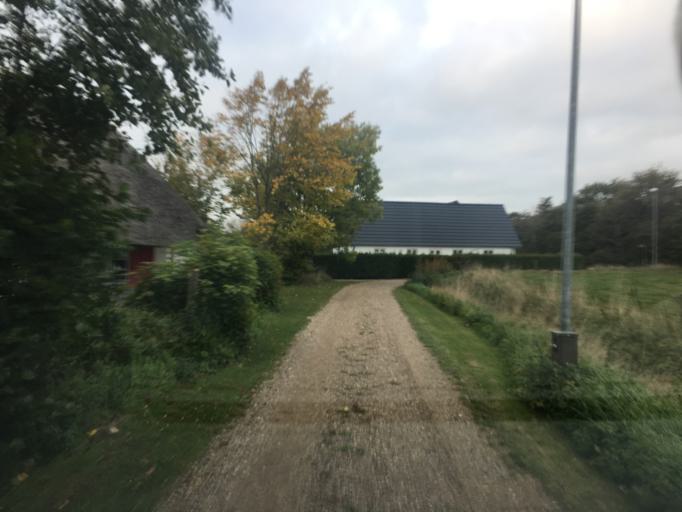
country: DE
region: Schleswig-Holstein
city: Aventoft
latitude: 54.9700
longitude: 8.7704
